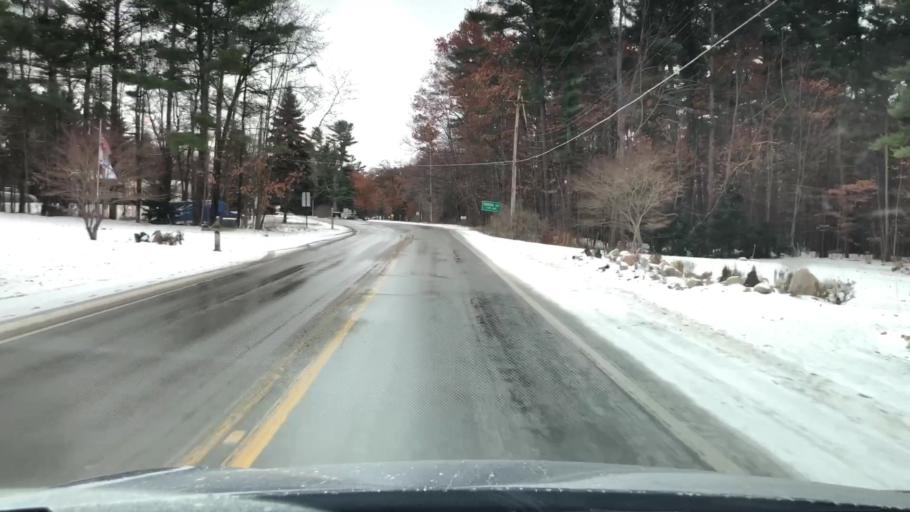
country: US
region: Michigan
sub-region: Grand Traverse County
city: Traverse City
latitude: 44.7751
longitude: -85.5912
